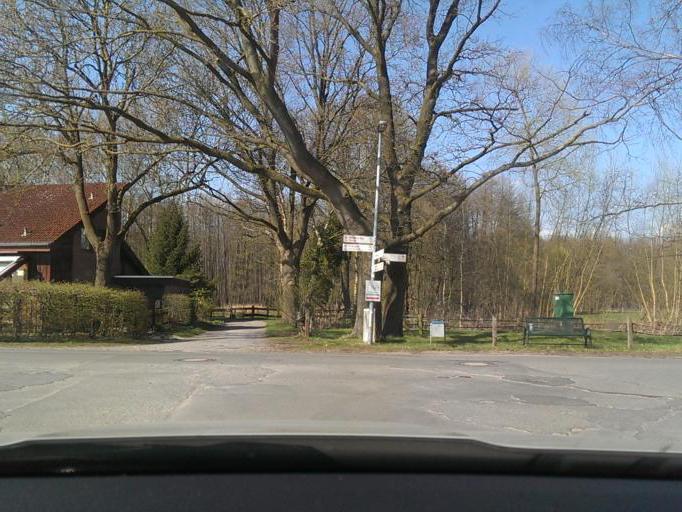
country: DE
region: Lower Saxony
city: Elze
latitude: 52.5632
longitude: 9.7338
